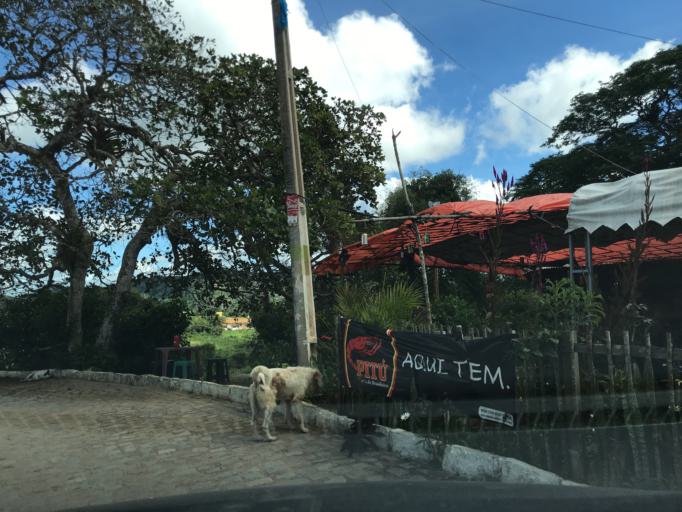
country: BR
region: Pernambuco
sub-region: Bezerros
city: Bezerros
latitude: -8.1640
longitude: -35.7692
